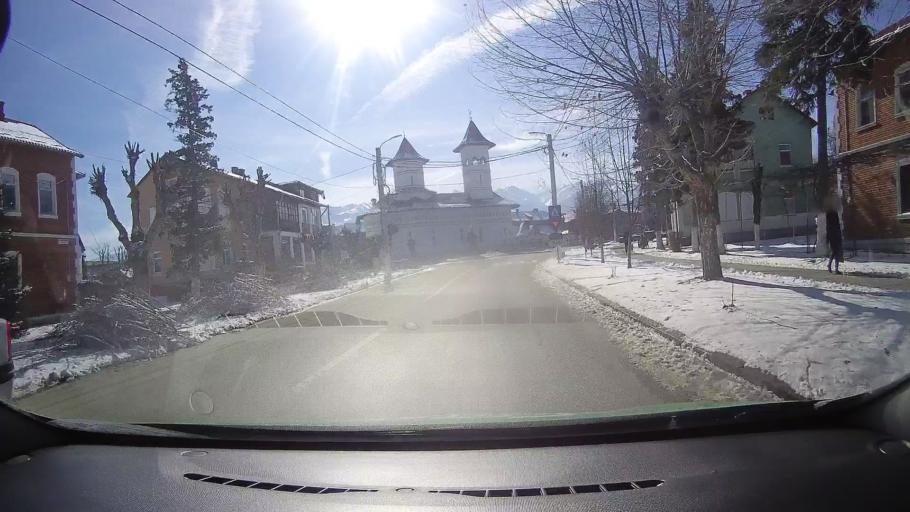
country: RO
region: Brasov
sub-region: Oras Victoria
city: Victoria
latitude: 45.7262
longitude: 24.7018
